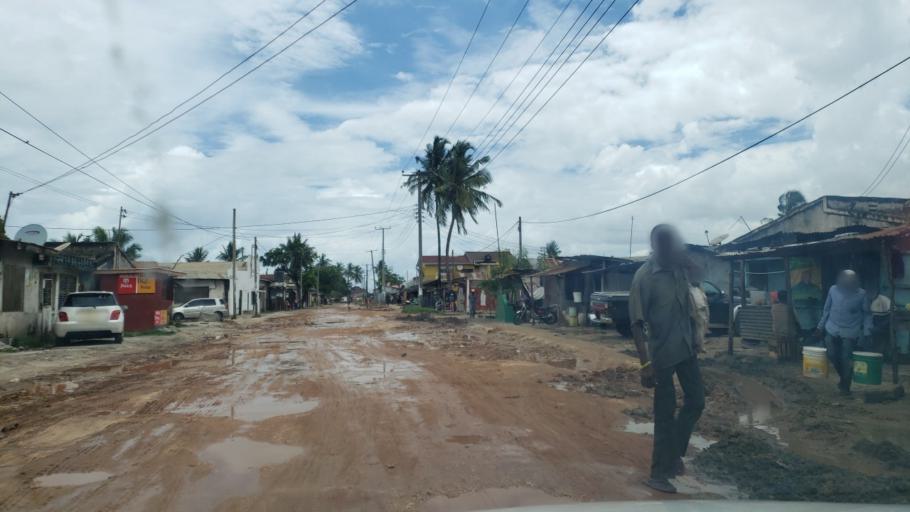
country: TZ
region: Dar es Salaam
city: Magomeni
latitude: -6.8067
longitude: 39.2300
